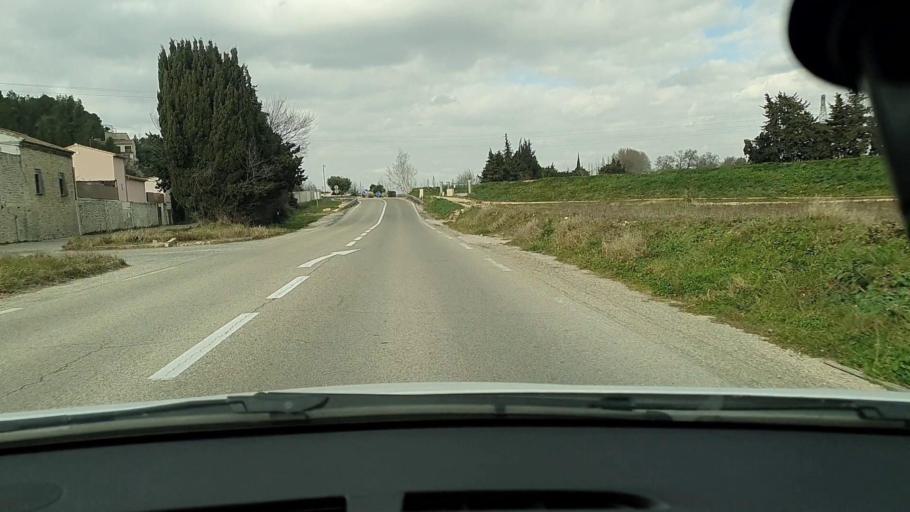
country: FR
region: Languedoc-Roussillon
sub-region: Departement du Gard
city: Beaucaire
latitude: 43.8191
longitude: 4.6293
